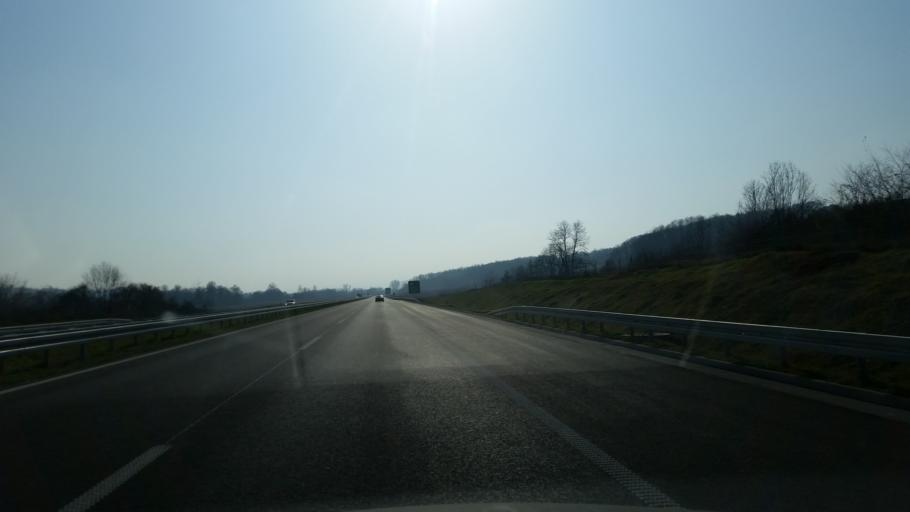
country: RS
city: Prislonica
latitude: 43.9406
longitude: 20.4002
